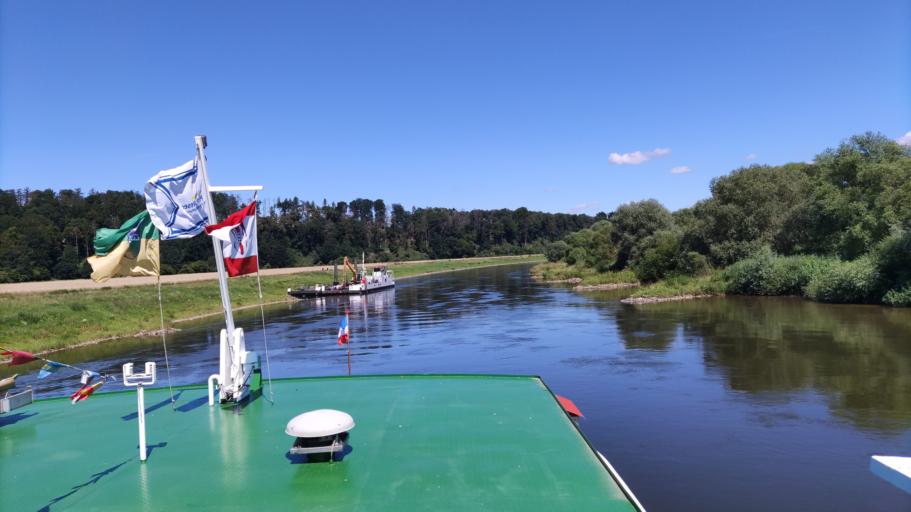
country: DE
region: Lower Saxony
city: Furstenberg
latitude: 51.7173
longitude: 9.3889
